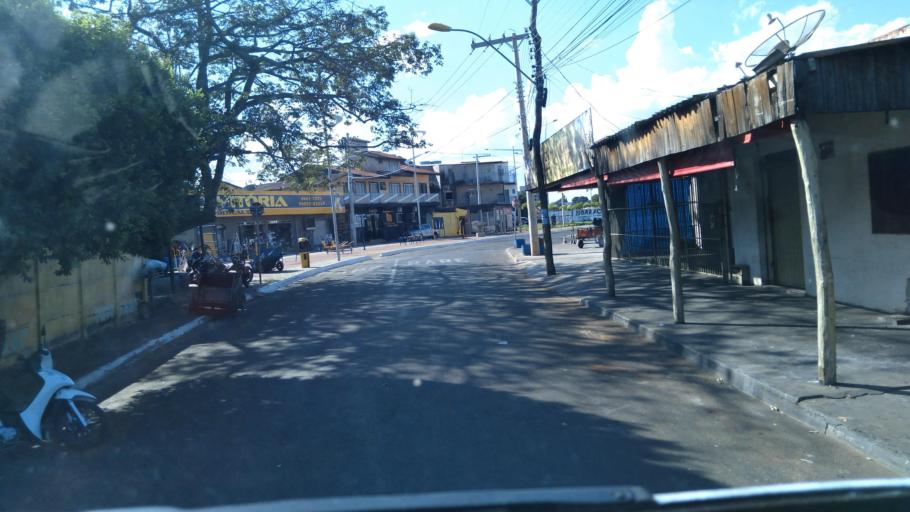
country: BR
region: Goias
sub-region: Mineiros
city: Mineiros
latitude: -17.5562
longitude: -52.5499
